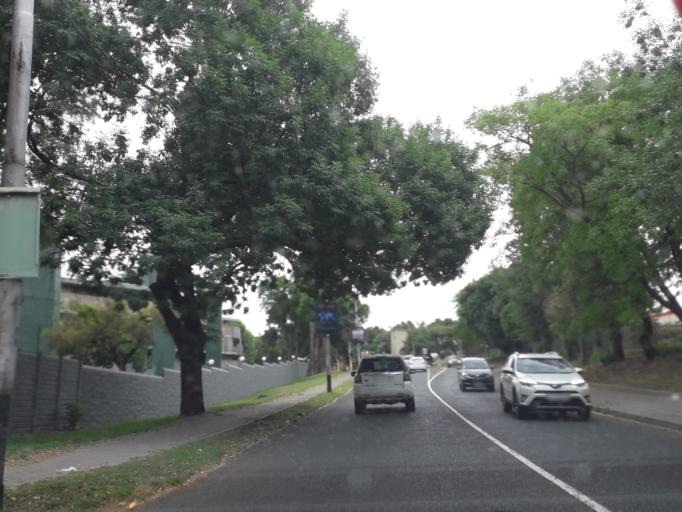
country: ZA
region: Gauteng
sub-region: City of Johannesburg Metropolitan Municipality
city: Johannesburg
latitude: -26.1477
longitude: 28.0775
